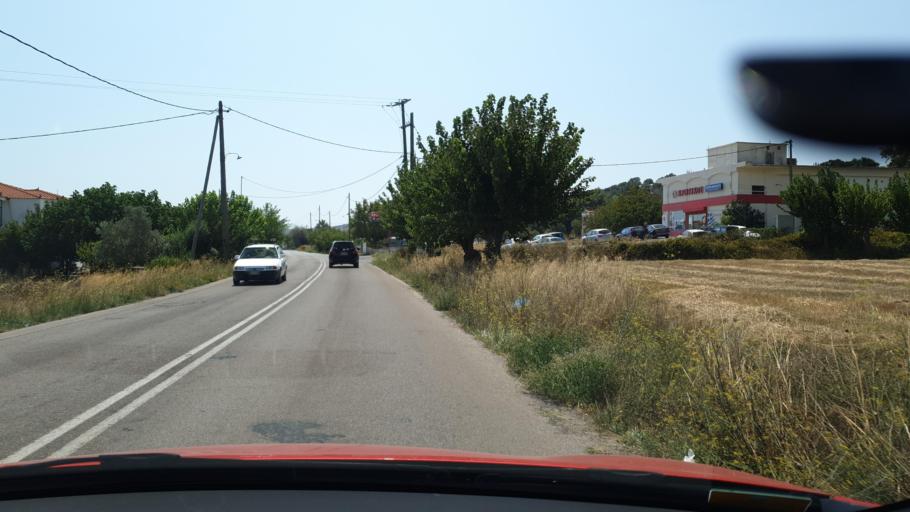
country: GR
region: Central Greece
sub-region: Nomos Evvoias
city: Oxilithos
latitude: 38.5062
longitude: 24.1095
